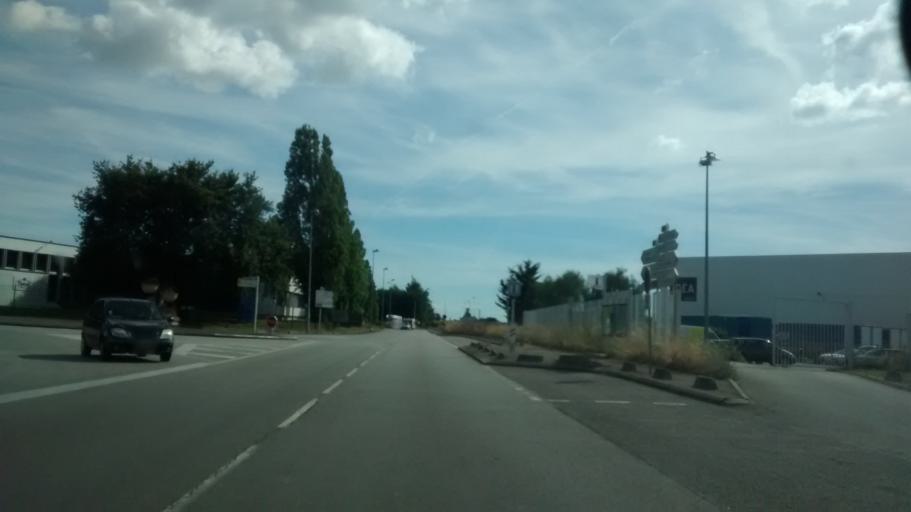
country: FR
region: Pays de la Loire
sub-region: Departement de la Loire-Atlantique
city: Bouguenais
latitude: 47.1555
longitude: -1.5981
